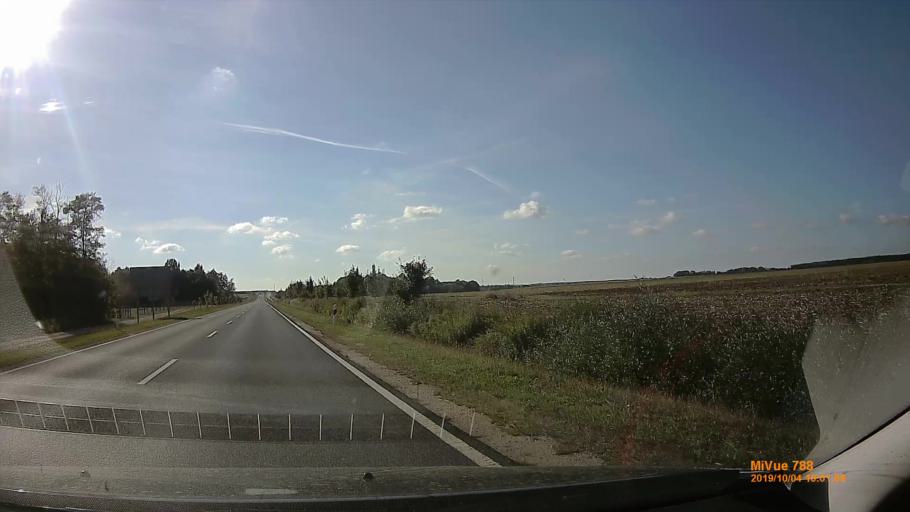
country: HU
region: Somogy
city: Kaposvar
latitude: 46.4110
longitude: 17.7710
